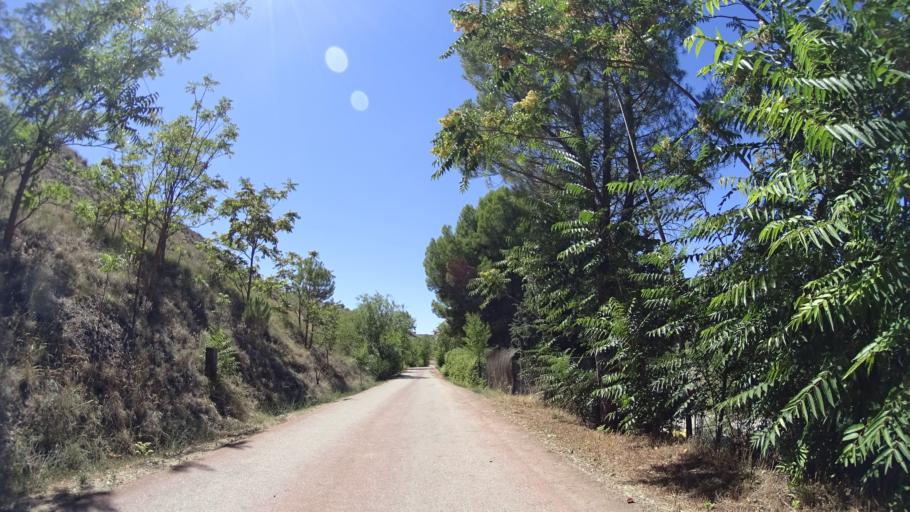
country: ES
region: Madrid
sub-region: Provincia de Madrid
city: Tielmes
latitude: 40.2397
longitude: -3.3070
